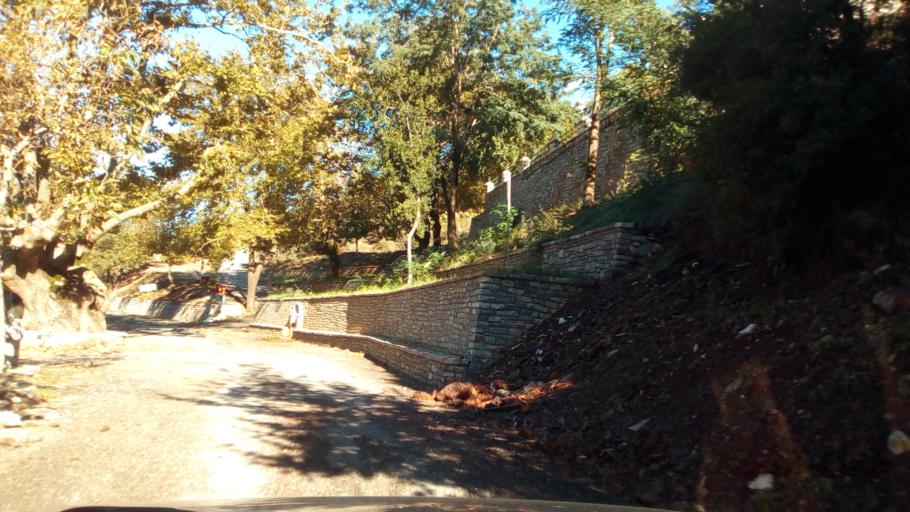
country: GR
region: West Greece
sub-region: Nomos Aitolias kai Akarnanias
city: Nafpaktos
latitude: 38.5581
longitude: 21.8558
